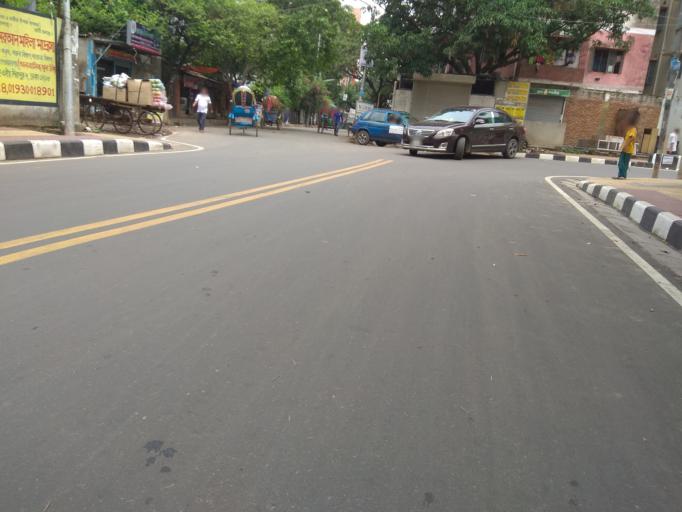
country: BD
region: Dhaka
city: Azimpur
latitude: 23.8024
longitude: 90.3574
